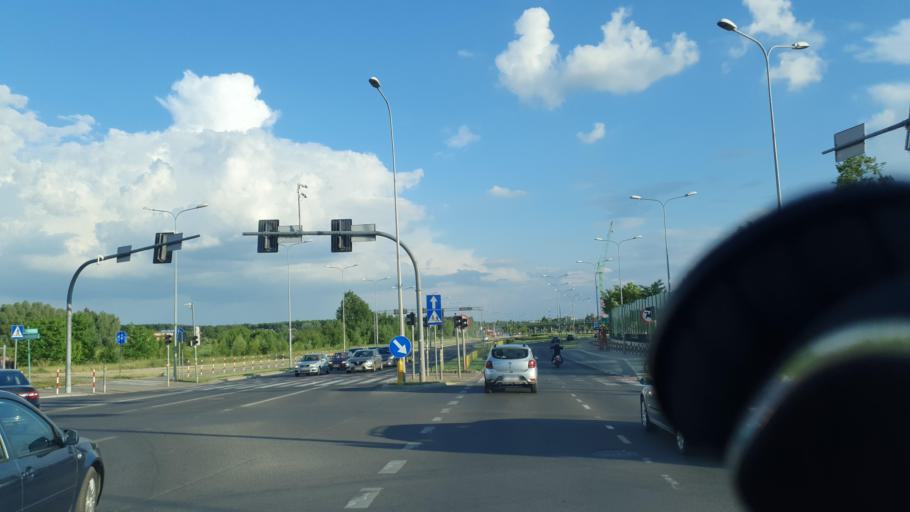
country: PL
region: Podlasie
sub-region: Bialystok
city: Bialystok
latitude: 53.1441
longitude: 23.2018
